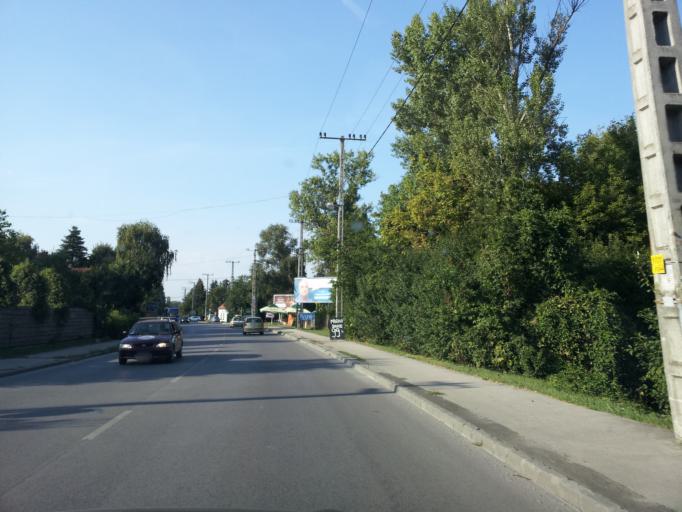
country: HU
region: Pest
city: Leanyfalu
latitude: 47.6929
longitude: 19.0881
